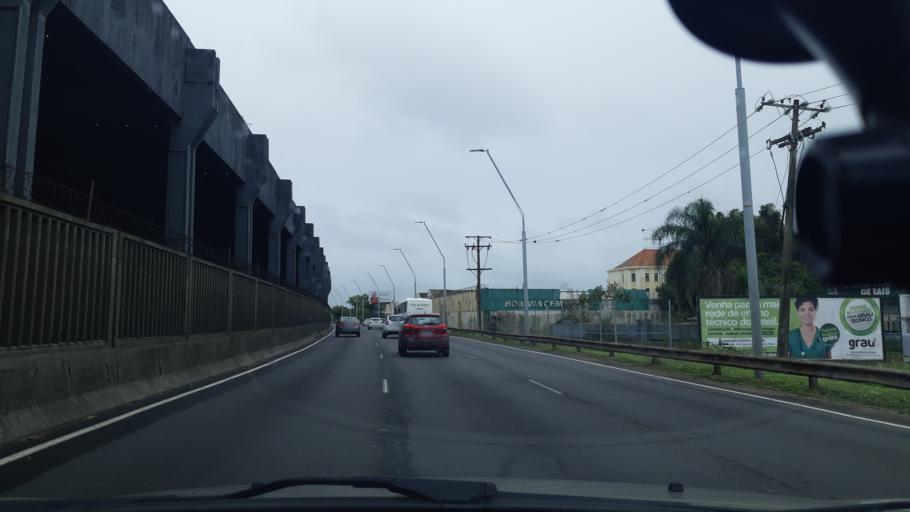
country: BR
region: Rio Grande do Sul
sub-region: Porto Alegre
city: Porto Alegre
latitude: -30.0069
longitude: -51.2095
